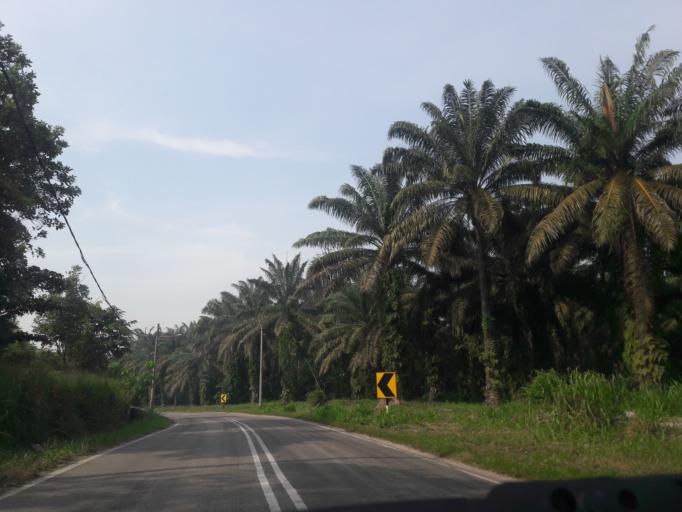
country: MY
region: Kedah
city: Kulim
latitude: 5.3480
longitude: 100.5194
